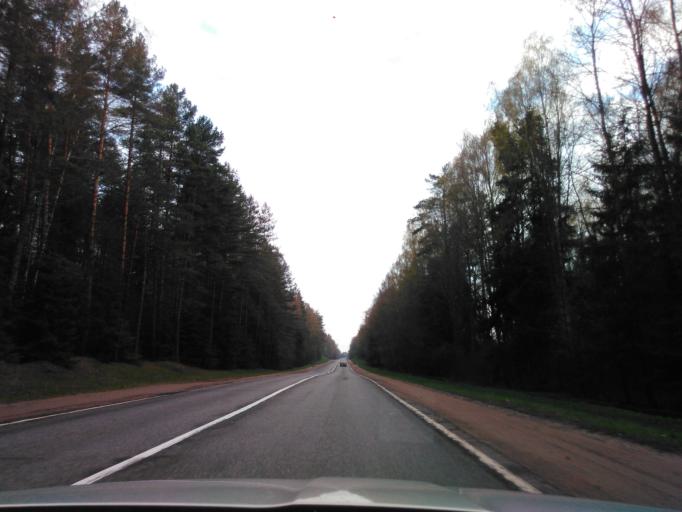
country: BY
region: Minsk
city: Lahoysk
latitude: 54.3091
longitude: 27.8756
